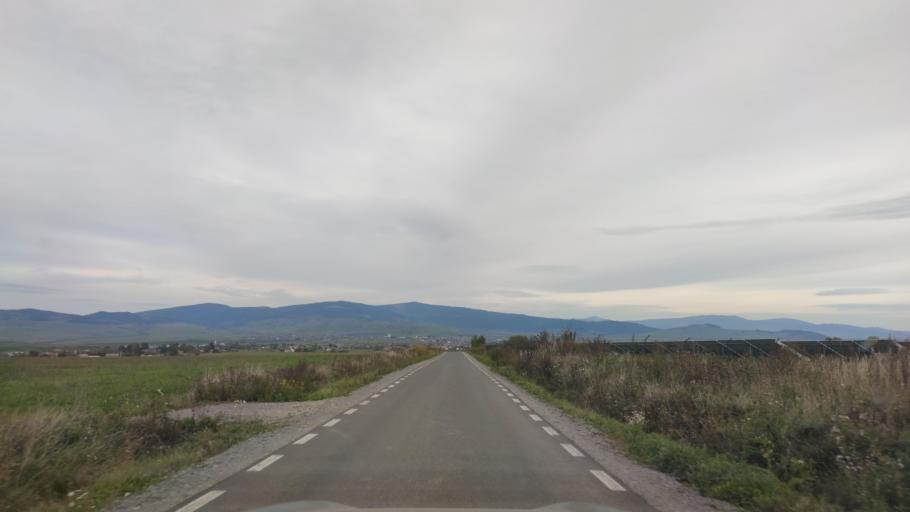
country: RO
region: Harghita
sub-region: Comuna Remetea
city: Remetea
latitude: 46.8069
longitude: 25.4178
